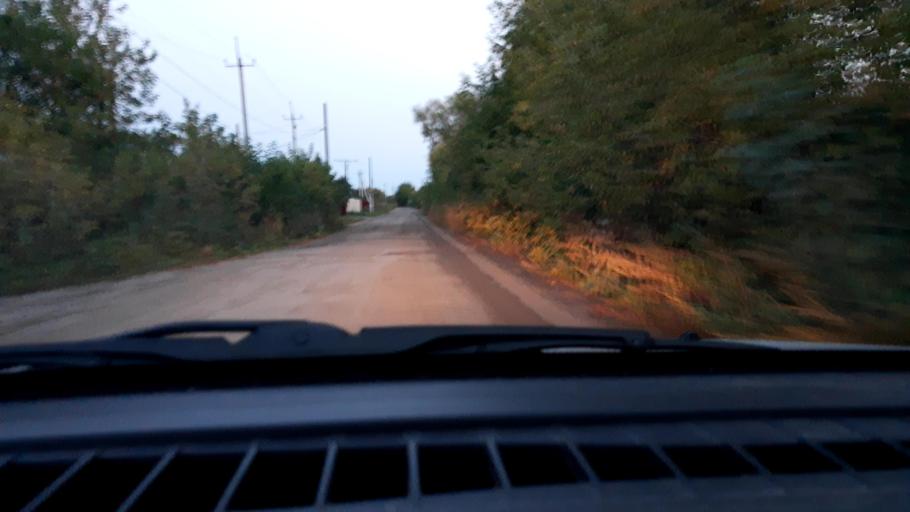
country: RU
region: Nizjnij Novgorod
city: Gorbatovka
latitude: 56.2583
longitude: 43.8288
